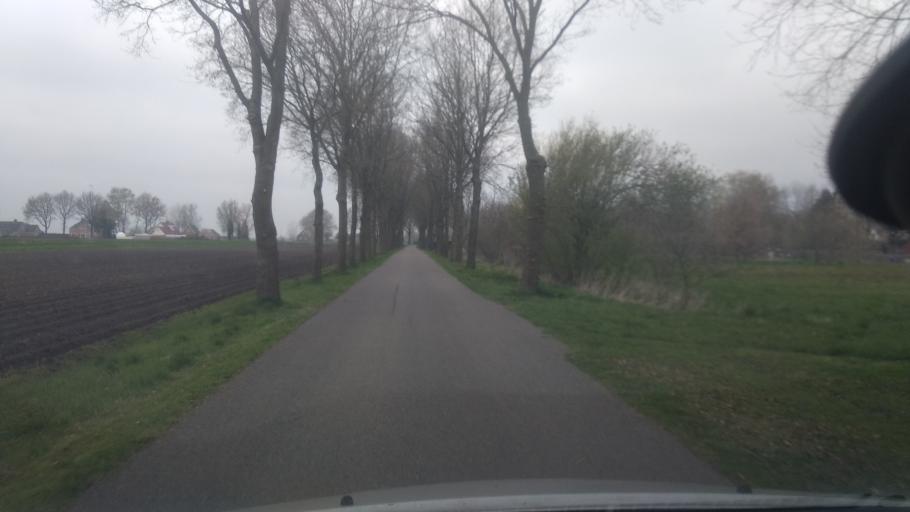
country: NL
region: Groningen
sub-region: Gemeente Stadskanaal
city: Stadskanaal
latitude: 52.9476
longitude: 6.9904
